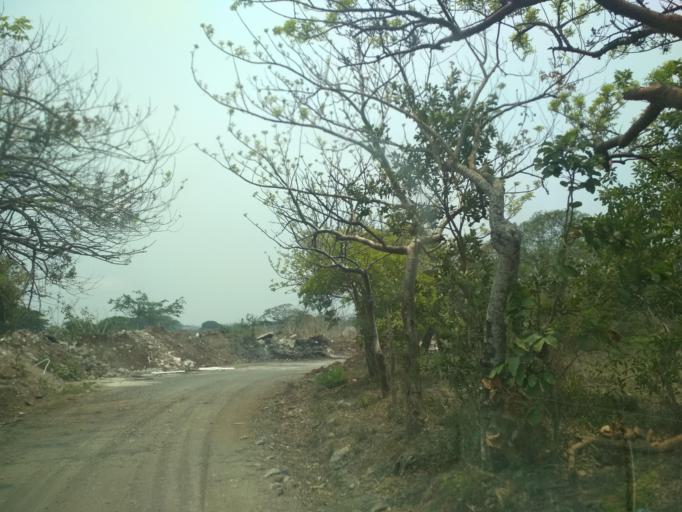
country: MX
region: Veracruz
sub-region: Veracruz
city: Oasis
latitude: 19.1919
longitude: -96.2453
